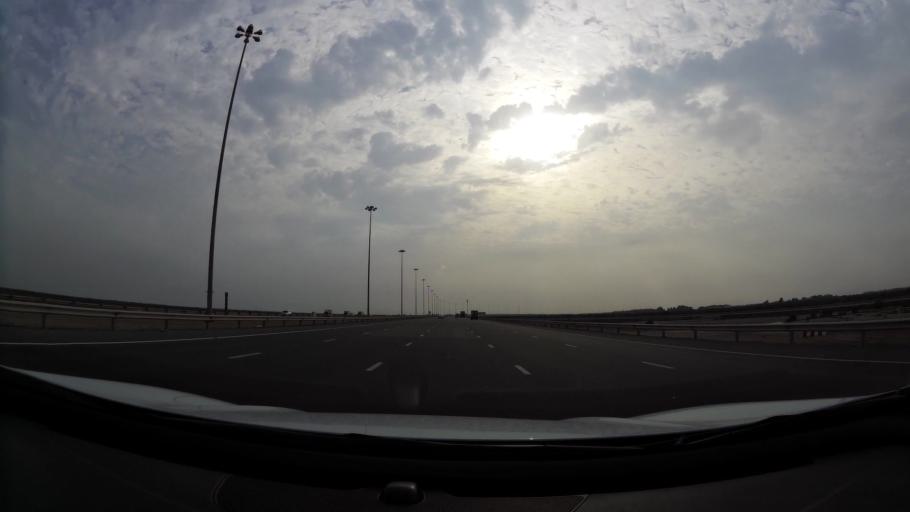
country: AE
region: Abu Dhabi
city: Abu Dhabi
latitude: 24.5477
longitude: 54.4661
